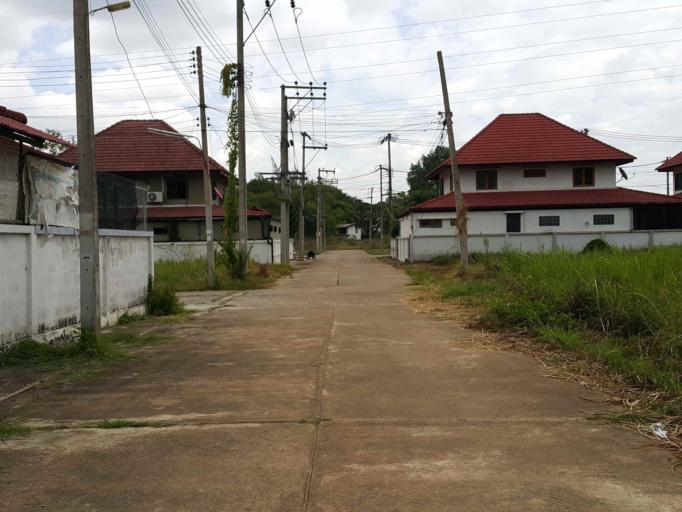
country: TH
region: Chiang Mai
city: Chiang Mai
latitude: 18.7701
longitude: 99.0212
